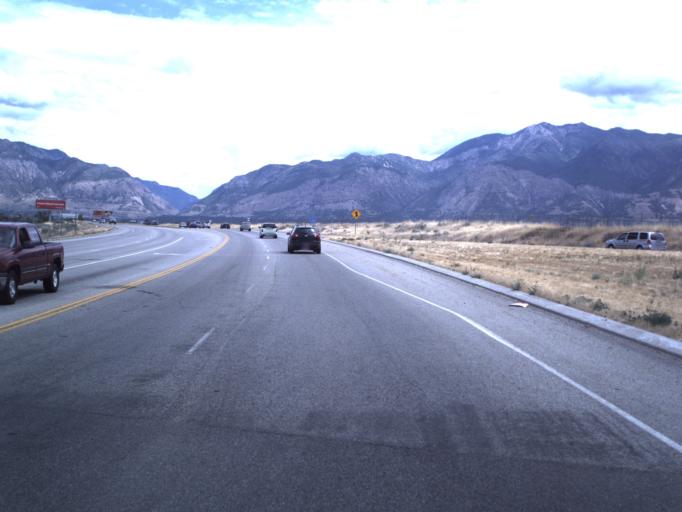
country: US
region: Utah
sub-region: Weber County
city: West Haven
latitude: 41.1987
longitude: -112.0253
